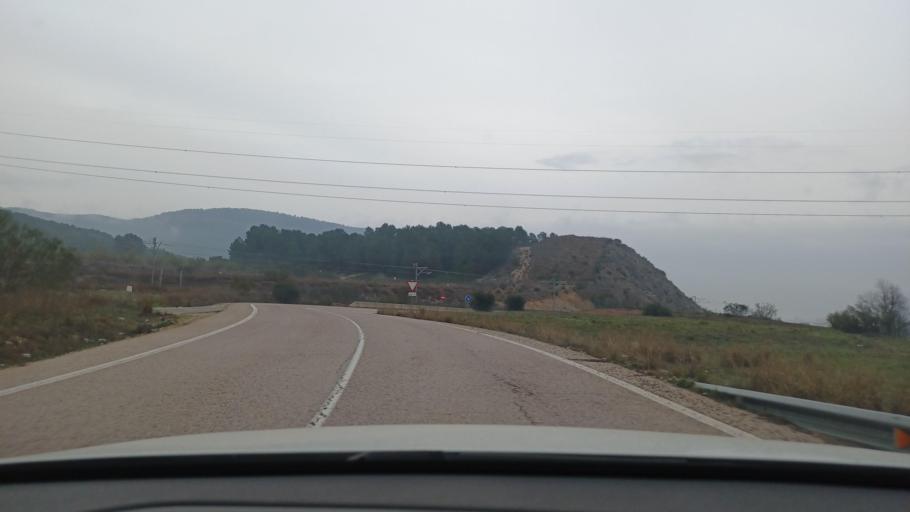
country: ES
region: Valencia
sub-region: Provincia de Valencia
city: La Font de la Figuera
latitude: 38.8354
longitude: -0.8678
